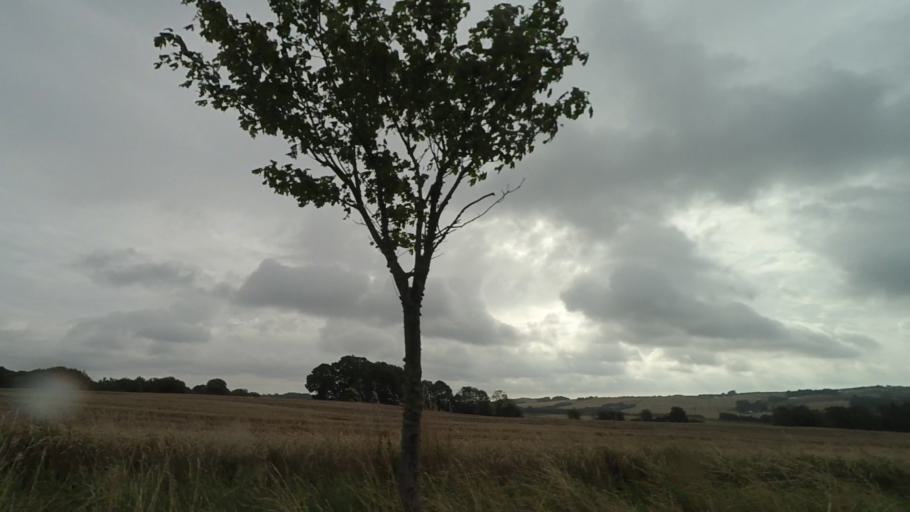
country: DK
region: Central Jutland
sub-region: Syddjurs Kommune
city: Ronde
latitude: 56.3169
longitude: 10.4599
